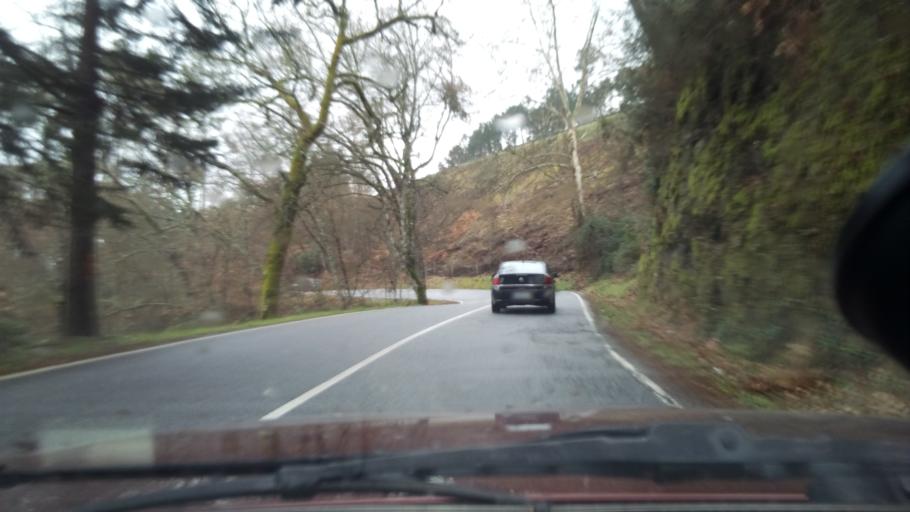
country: PT
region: Viseu
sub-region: Mangualde
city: Mangualde
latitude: 40.6339
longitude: -7.8111
